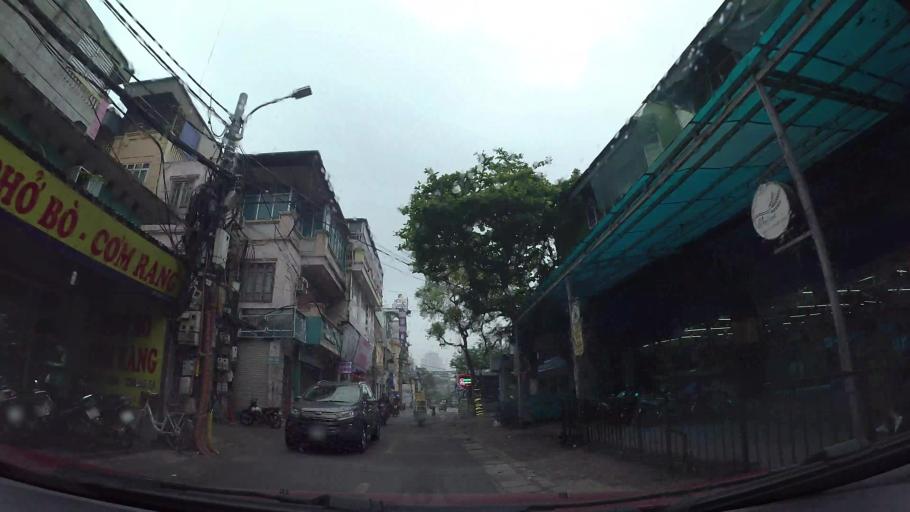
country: VN
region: Ha Noi
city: Dong Da
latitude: 21.0131
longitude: 105.8229
